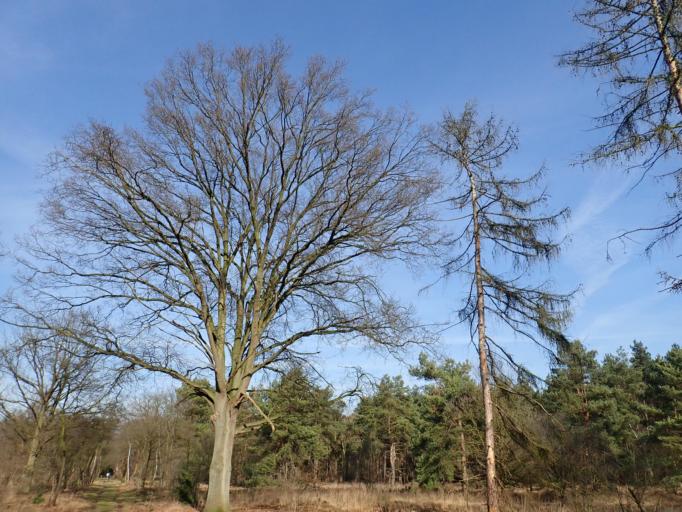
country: BE
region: Flanders
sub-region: Provincie Antwerpen
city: Stabroek
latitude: 51.3536
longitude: 4.3526
